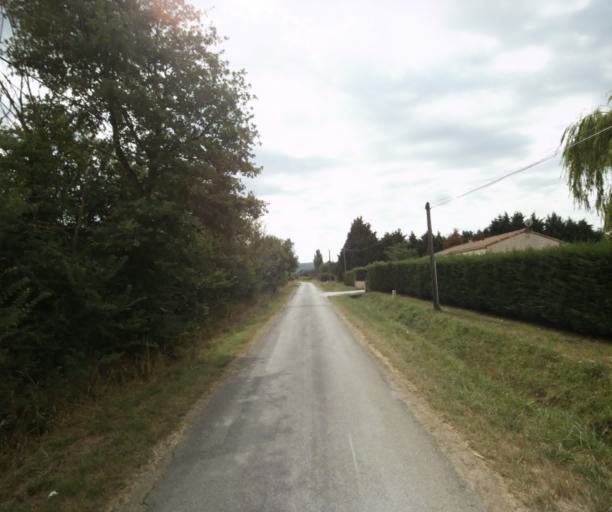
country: FR
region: Midi-Pyrenees
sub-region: Departement de la Haute-Garonne
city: Saint-Felix-Lauragais
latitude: 43.4323
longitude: 1.9408
